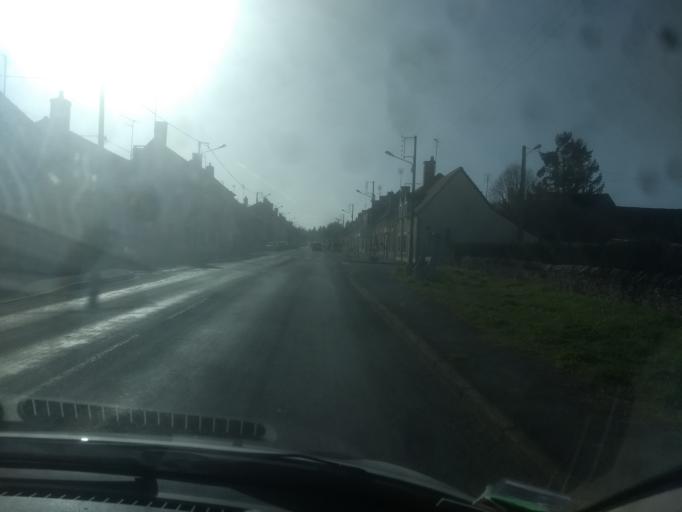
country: FR
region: Centre
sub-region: Departement du Cher
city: Orval
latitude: 46.7712
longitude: 2.4328
